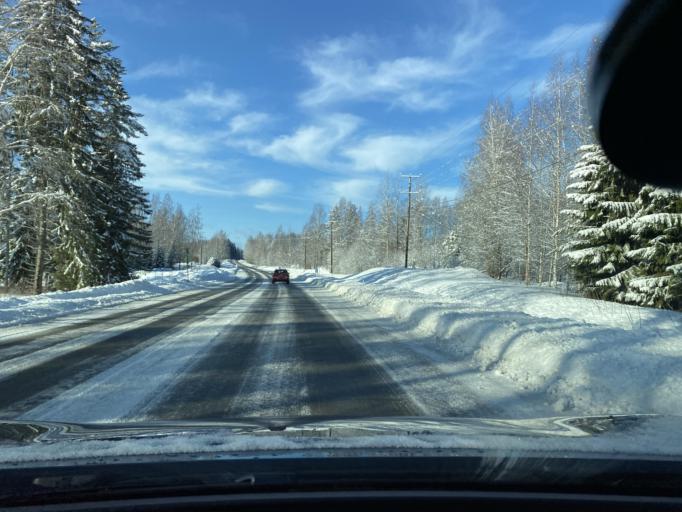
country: FI
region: Southern Savonia
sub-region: Mikkeli
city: Kangasniemi
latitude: 62.0149
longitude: 26.6191
